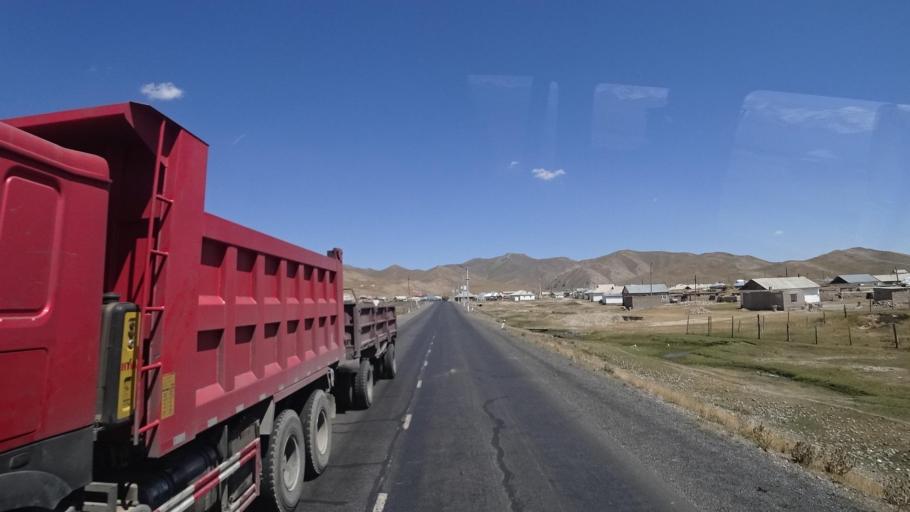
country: KG
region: Osh
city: Gul'cha
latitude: 39.7209
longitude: 73.2460
